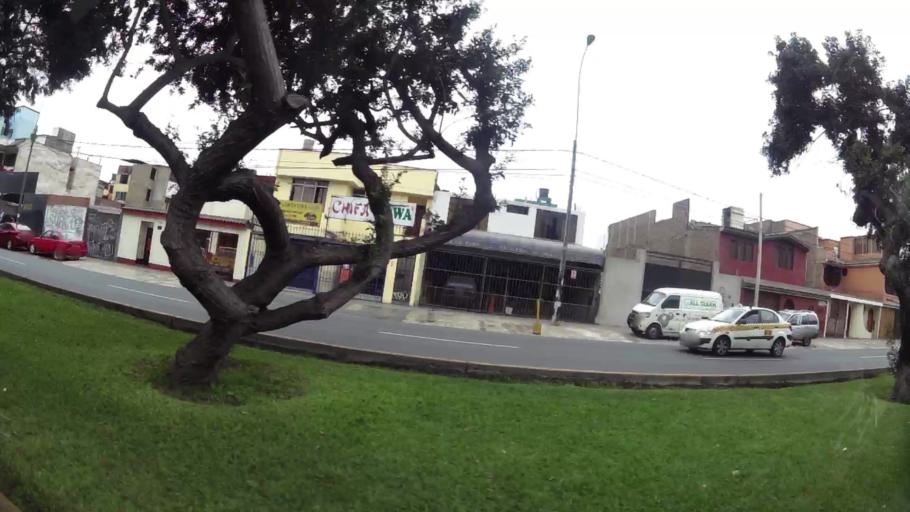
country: PE
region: Lima
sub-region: Lima
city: Surco
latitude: -12.1445
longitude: -76.9855
